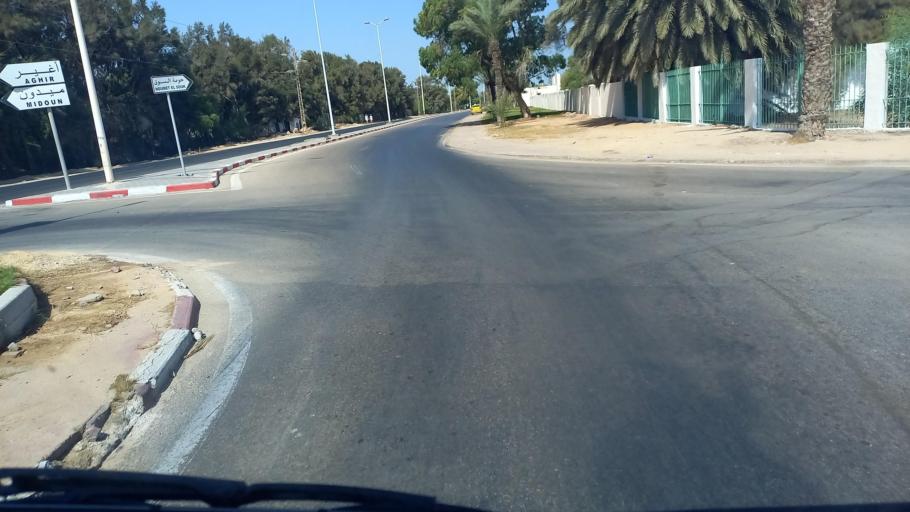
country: TN
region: Madanin
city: Midoun
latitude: 33.8264
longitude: 11.0161
